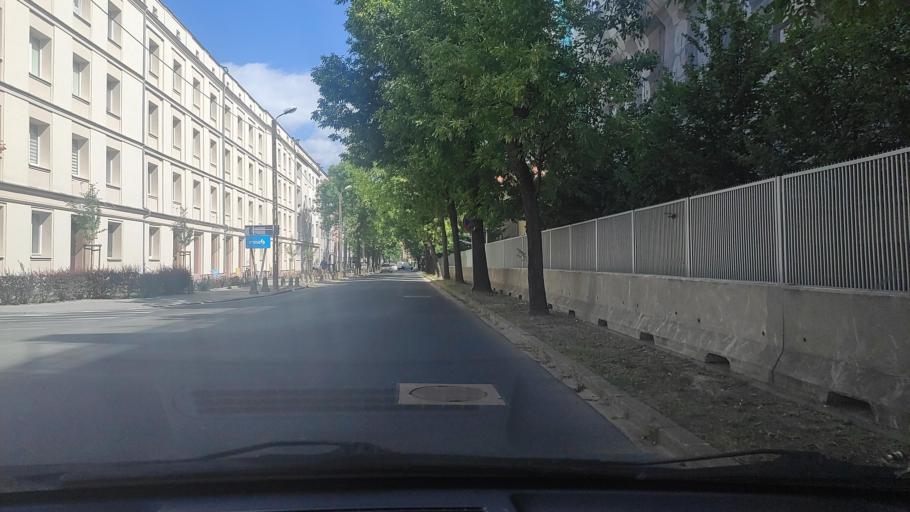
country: PL
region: Greater Poland Voivodeship
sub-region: Poznan
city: Poznan
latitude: 52.4068
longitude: 16.8938
